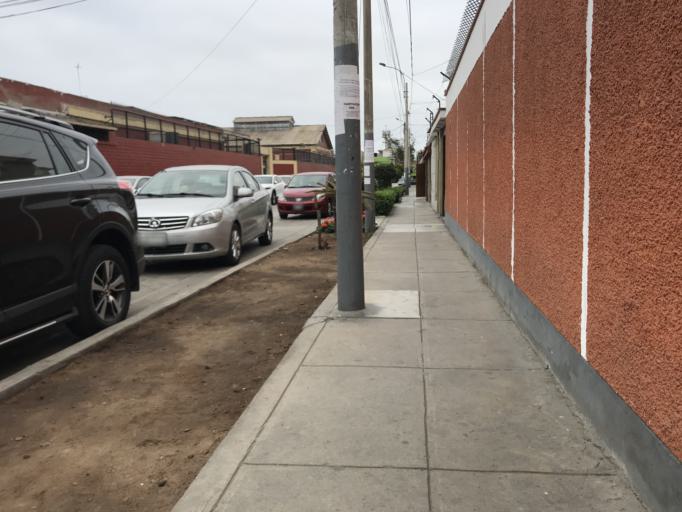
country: PE
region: Lima
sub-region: Lima
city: San Isidro
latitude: -12.0796
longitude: -77.0715
